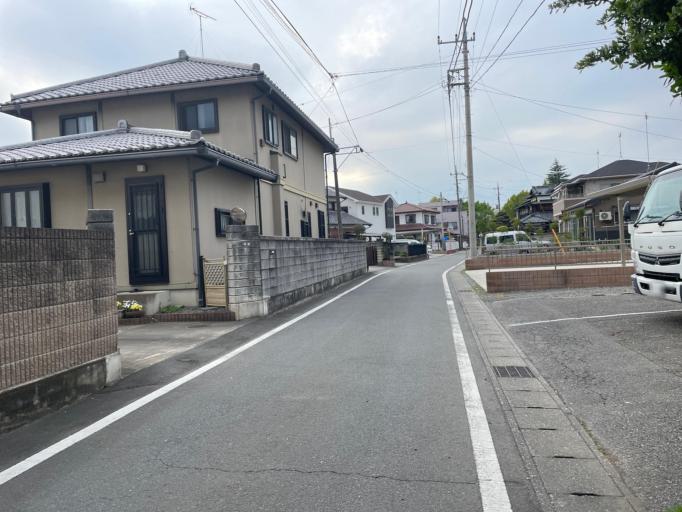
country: JP
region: Gunma
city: Sakai-nakajima
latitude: 36.2757
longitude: 139.2536
